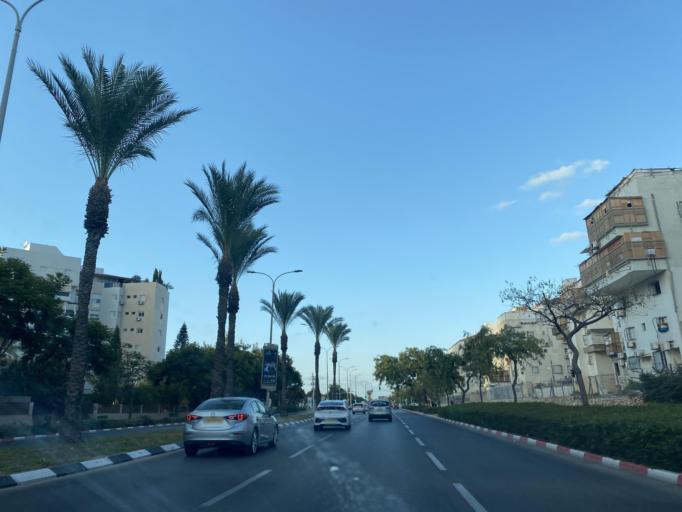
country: IL
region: Southern District
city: Ashdod
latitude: 31.7899
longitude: 34.6488
